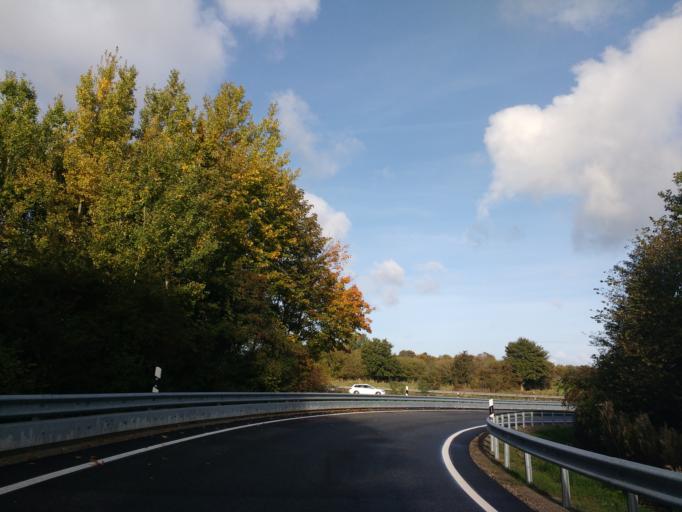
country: DE
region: Schleswig-Holstein
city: Altenkrempe
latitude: 54.1263
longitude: 10.8244
